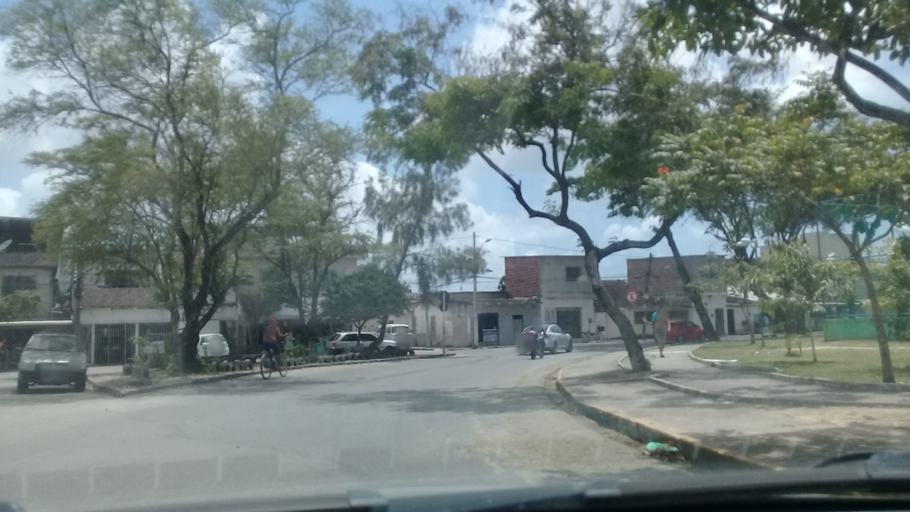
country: BR
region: Pernambuco
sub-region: Recife
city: Recife
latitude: -8.1054
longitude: -34.9201
